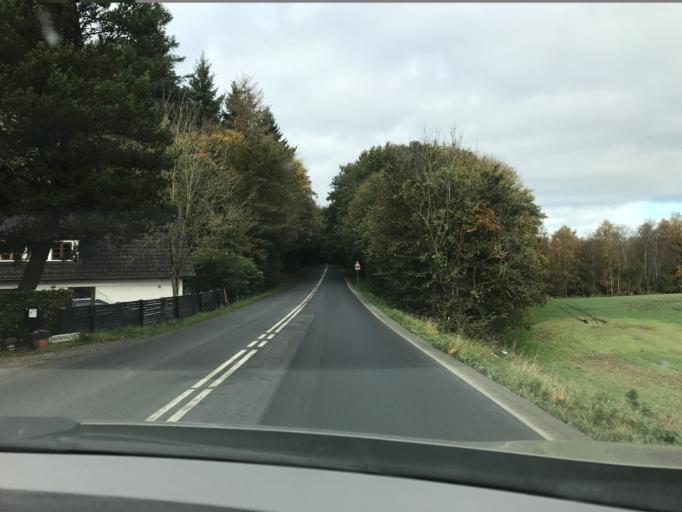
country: DK
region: South Denmark
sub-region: Kolding Kommune
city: Kolding
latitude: 55.5317
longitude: 9.4210
